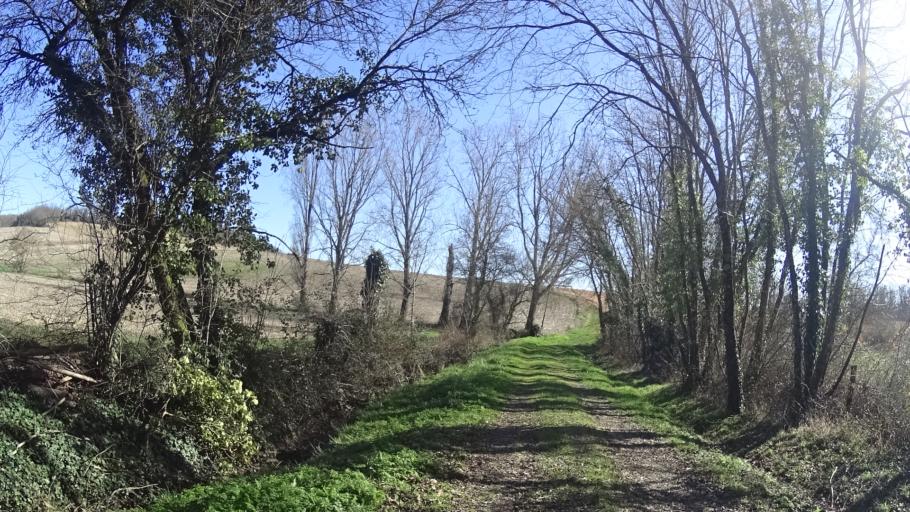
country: FR
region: Aquitaine
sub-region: Departement de la Dordogne
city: Saint-Aulaye
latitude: 45.2288
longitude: 0.1192
